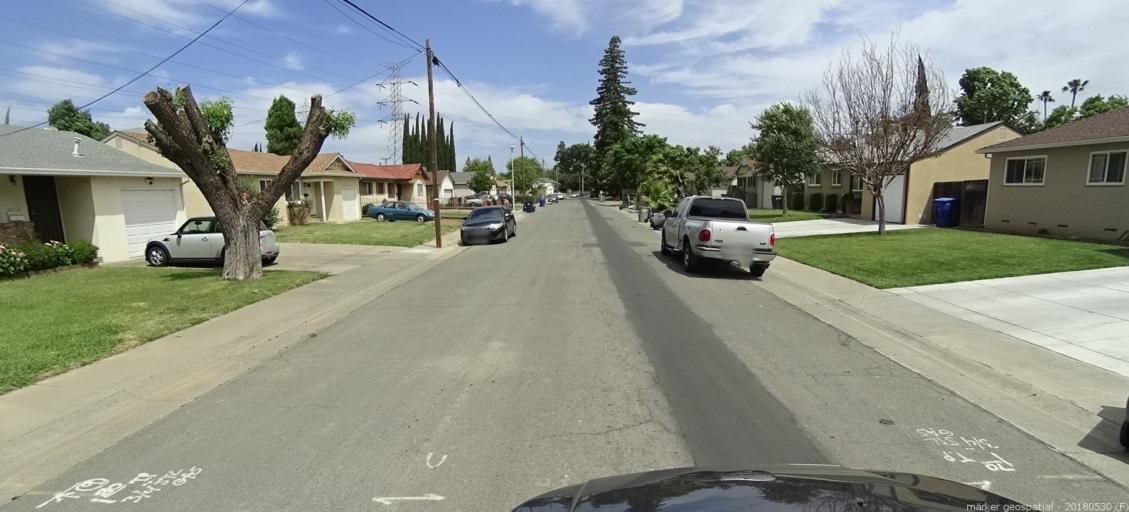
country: US
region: California
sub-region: Sacramento County
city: Sacramento
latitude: 38.6143
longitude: -121.4830
